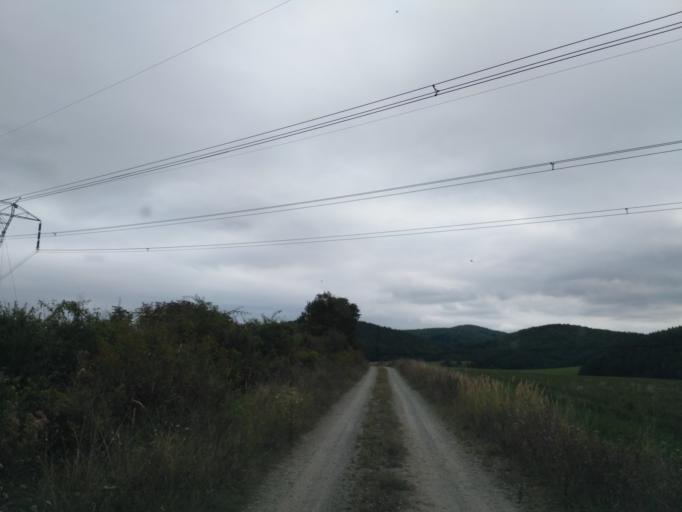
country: SK
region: Presovsky
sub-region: Okres Presov
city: Presov
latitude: 48.9072
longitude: 21.1575
